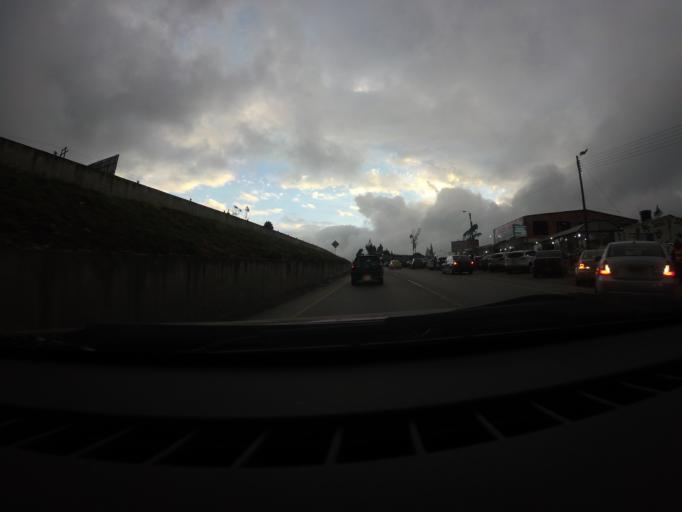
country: CO
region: Boyaca
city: Samaca
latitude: 5.4316
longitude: -73.4499
